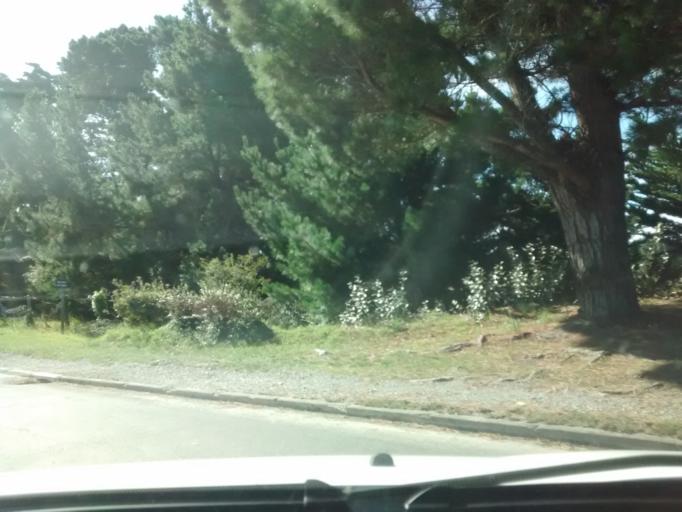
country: FR
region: Brittany
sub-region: Departement d'Ille-et-Vilaine
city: Saint-Briac-sur-Mer
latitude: 48.6157
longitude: -2.1370
